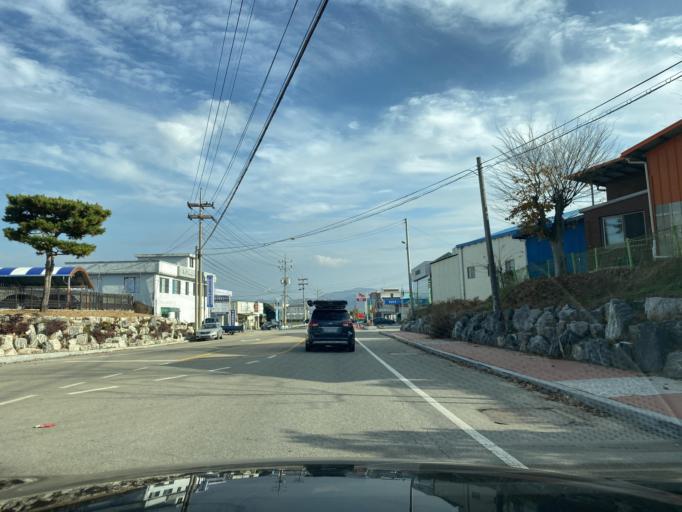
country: KR
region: Chungcheongnam-do
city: Yesan
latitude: 36.6880
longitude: 126.7975
